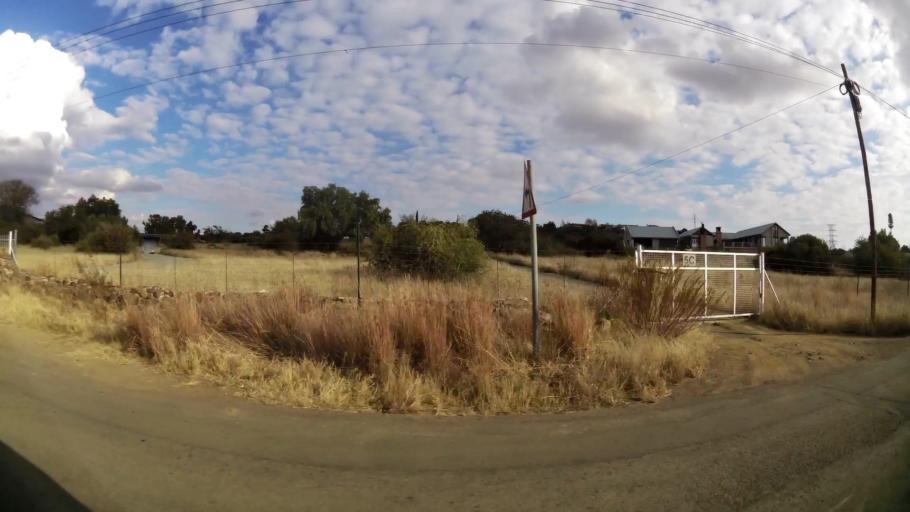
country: ZA
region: Orange Free State
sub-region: Mangaung Metropolitan Municipality
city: Bloemfontein
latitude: -29.0696
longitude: 26.2000
